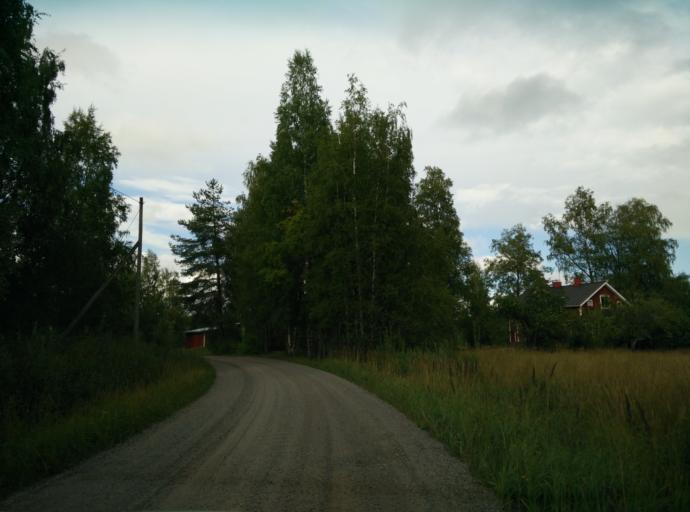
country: FI
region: Haeme
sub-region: Haemeenlinna
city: Kalvola
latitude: 61.1176
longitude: 24.1408
